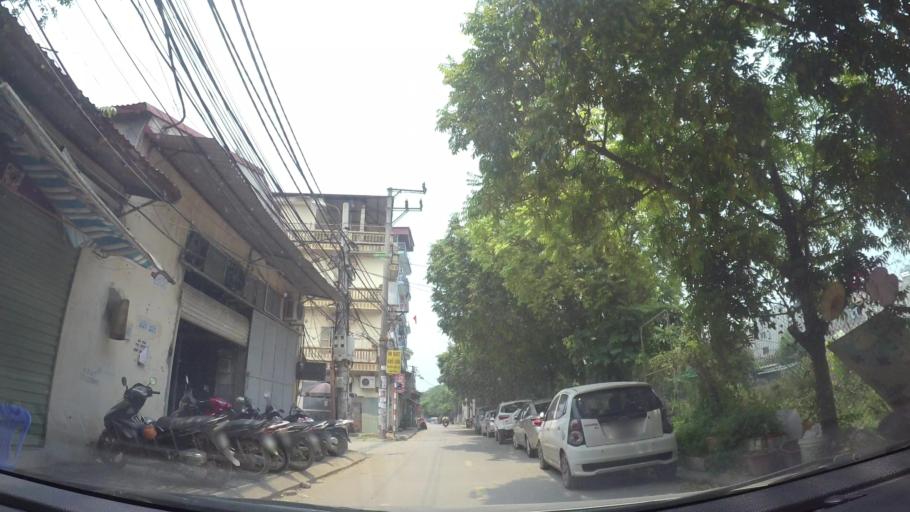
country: VN
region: Ha Noi
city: Ha Dong
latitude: 20.9943
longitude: 105.7735
